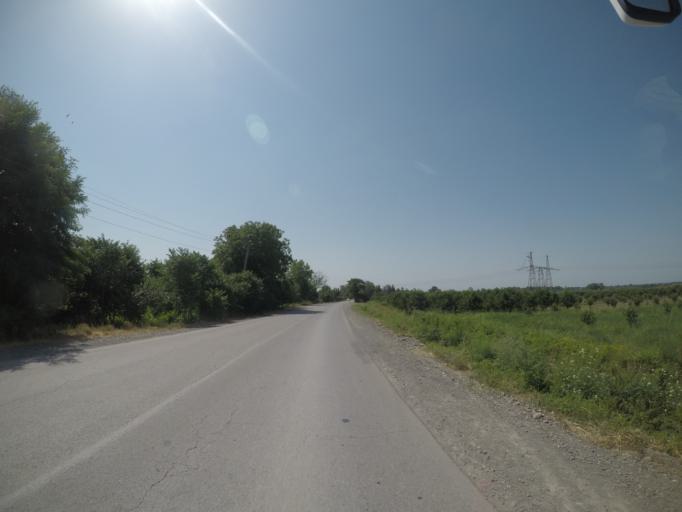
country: AZ
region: Agdas
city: Agdas
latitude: 40.7035
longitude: 47.5408
